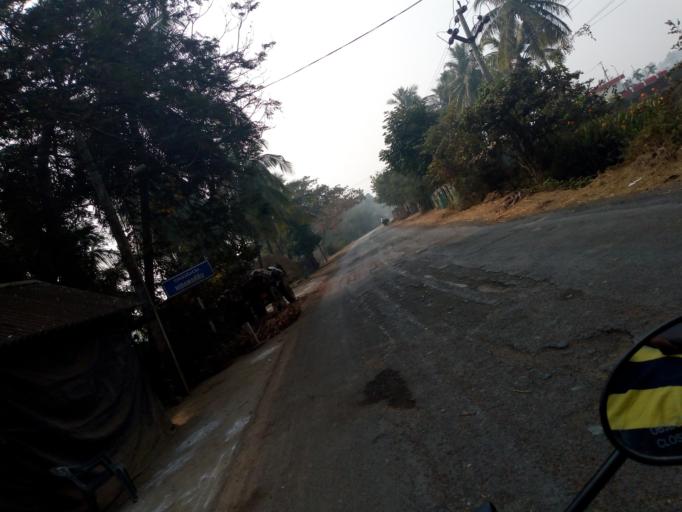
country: IN
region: Andhra Pradesh
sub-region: West Godavari
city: Pippara
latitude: 16.7317
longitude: 81.4195
